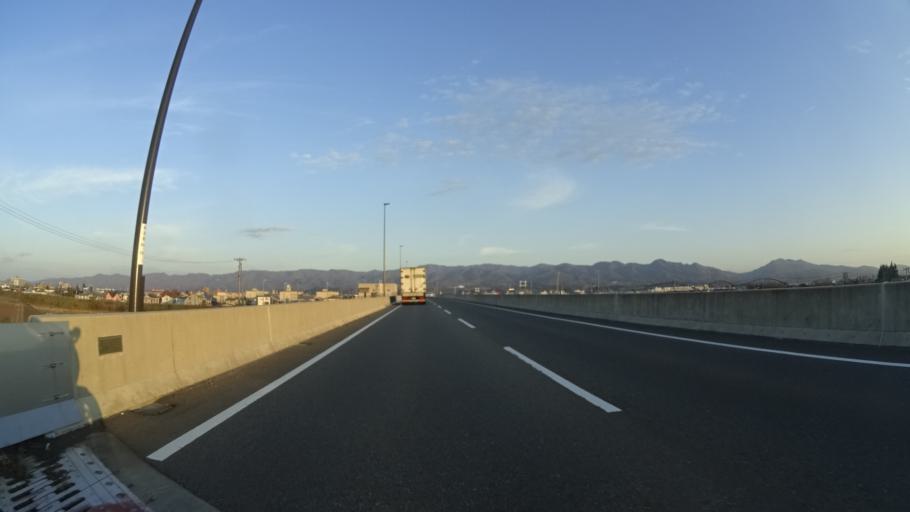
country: JP
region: Niigata
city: Nagaoka
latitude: 37.4286
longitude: 138.8304
